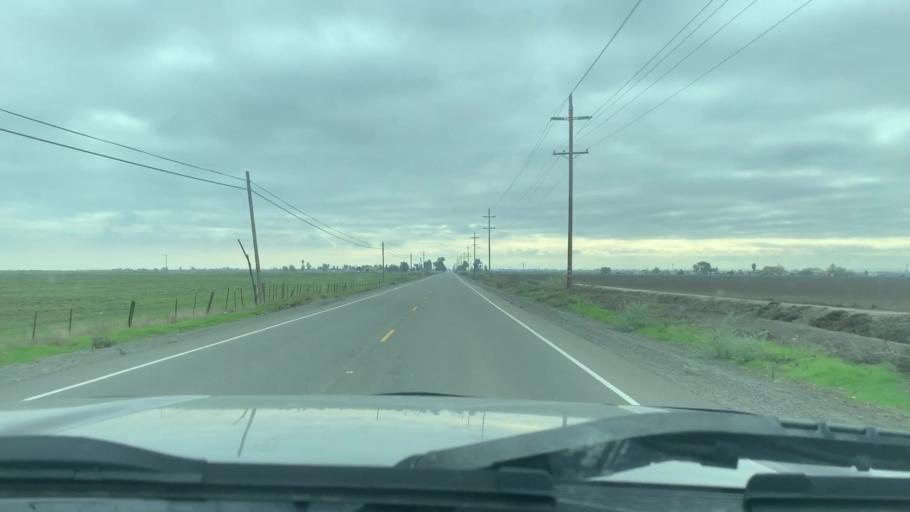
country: US
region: California
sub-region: Merced County
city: Los Banos
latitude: 37.1124
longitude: -120.8349
